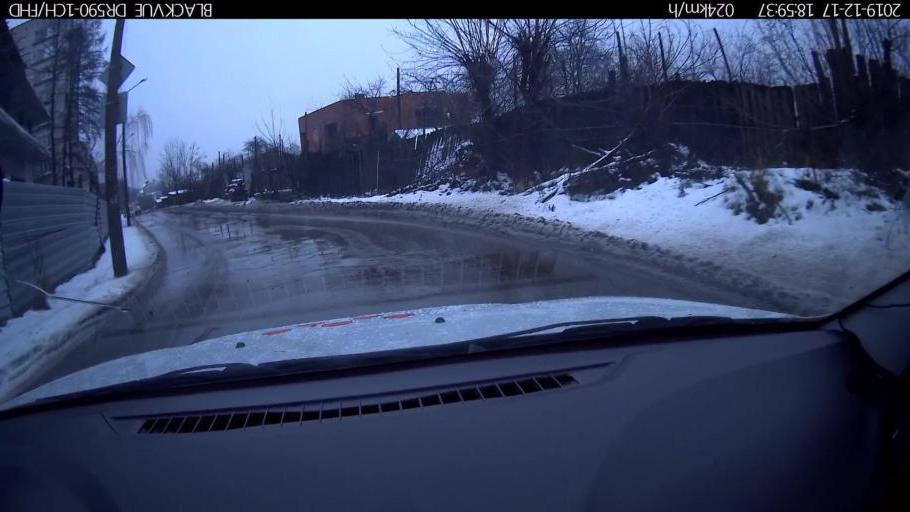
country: RU
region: Nizjnij Novgorod
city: Nizhniy Novgorod
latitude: 56.2914
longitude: 44.0154
